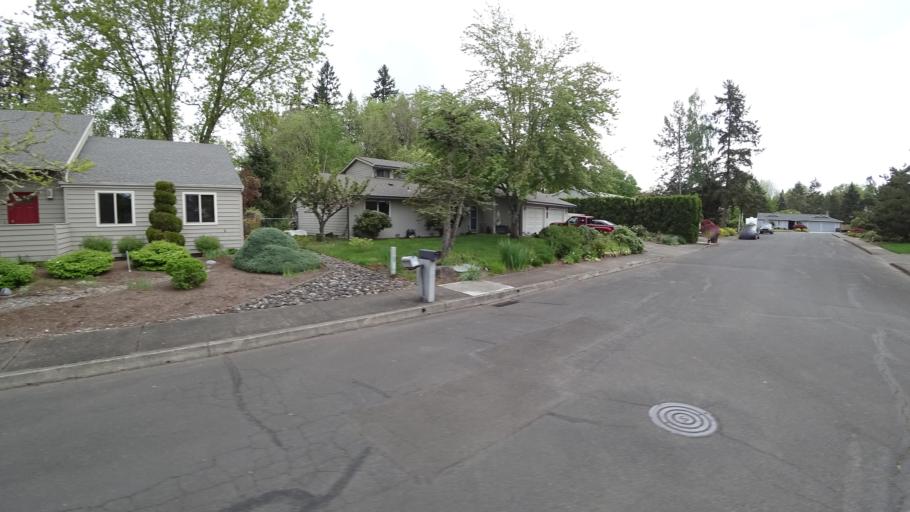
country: US
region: Oregon
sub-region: Washington County
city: Hillsboro
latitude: 45.5330
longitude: -122.9828
